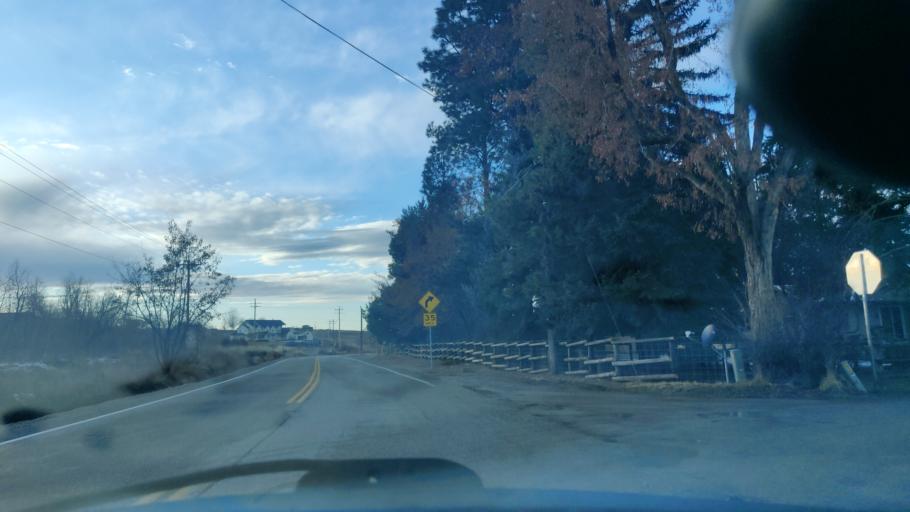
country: US
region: Idaho
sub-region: Ada County
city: Eagle
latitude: 43.7279
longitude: -116.2584
